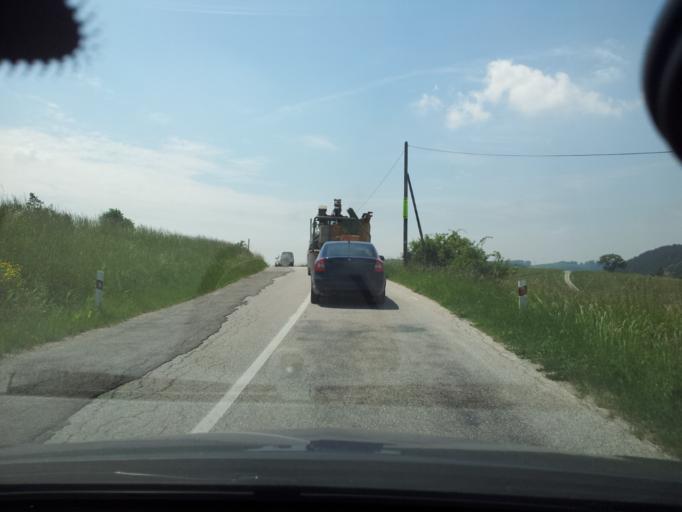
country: SK
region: Nitriansky
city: Partizanske
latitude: 48.5137
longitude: 18.4308
